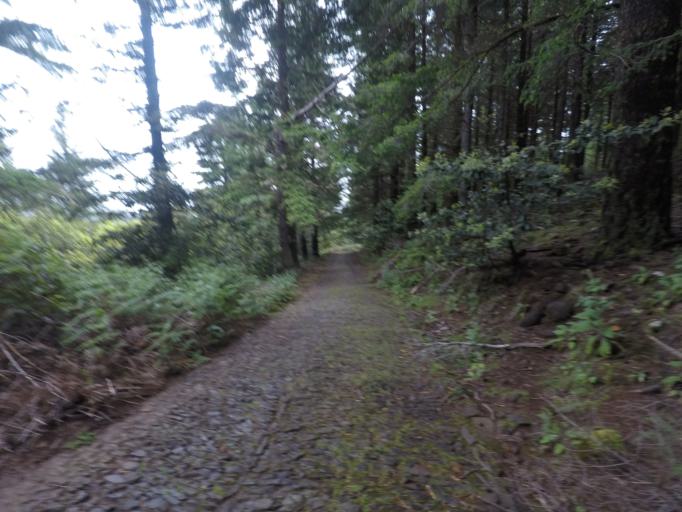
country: PT
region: Madeira
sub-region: Funchal
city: Nossa Senhora do Monte
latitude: 32.7167
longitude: -16.8863
